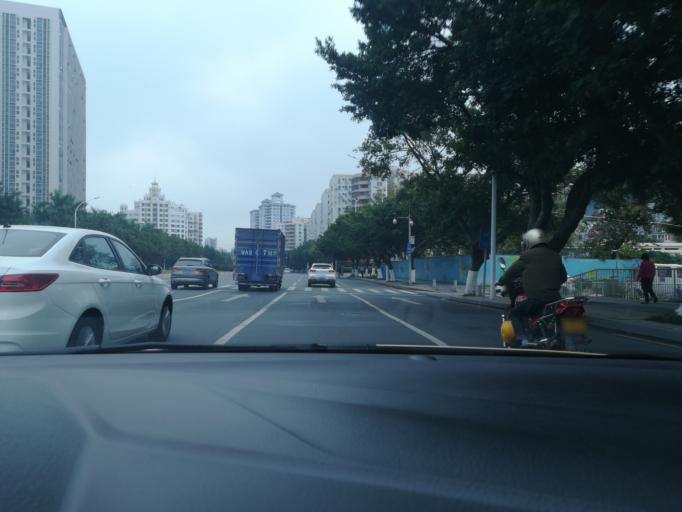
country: CN
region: Guangdong
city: Nansha
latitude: 22.8013
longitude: 113.5523
